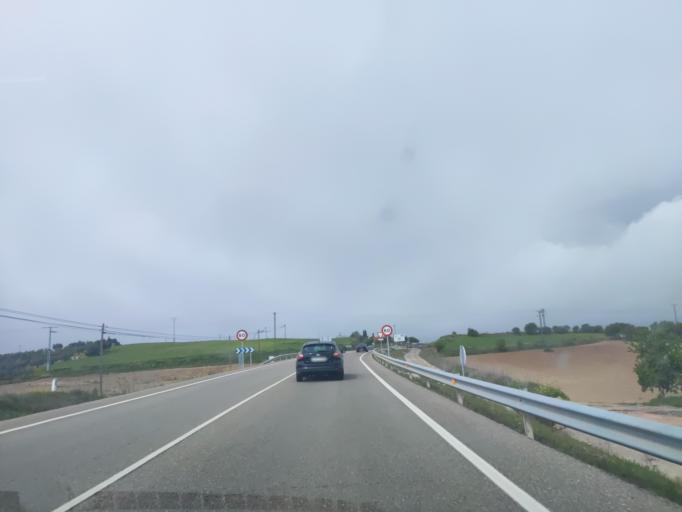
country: ES
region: Castille-La Mancha
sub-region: Province of Toledo
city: Olias del Rey
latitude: 39.9437
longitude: -4.0034
